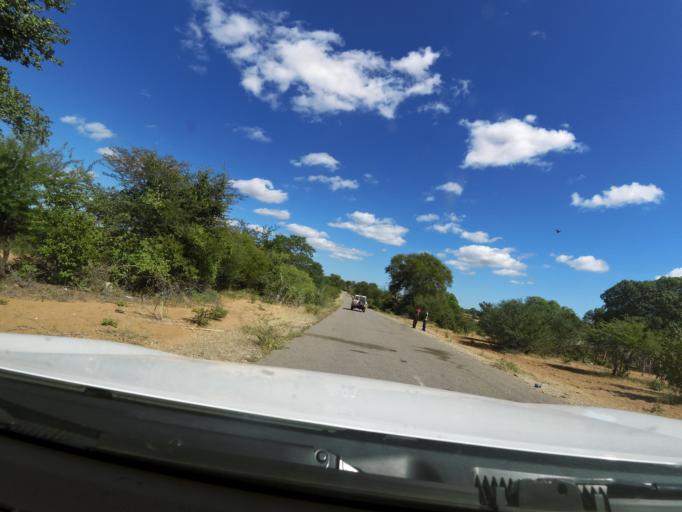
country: ZW
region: Matabeleland North
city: Kamativi Mine
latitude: -18.0071
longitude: 27.1474
